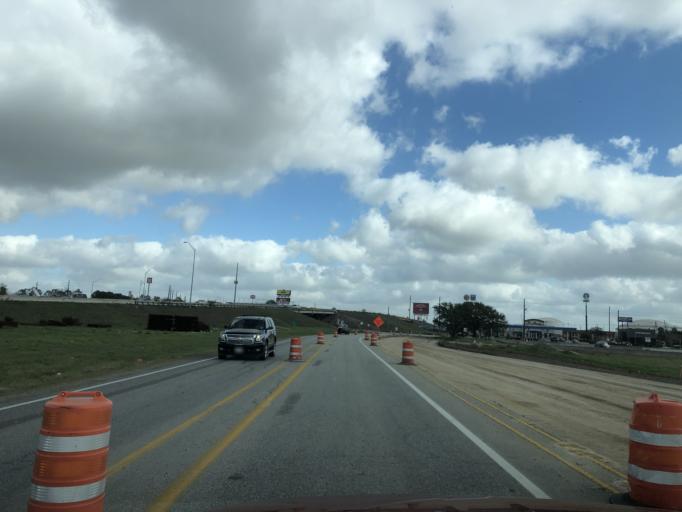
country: US
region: Texas
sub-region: Austin County
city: Sealy
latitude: 29.7631
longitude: -96.1546
